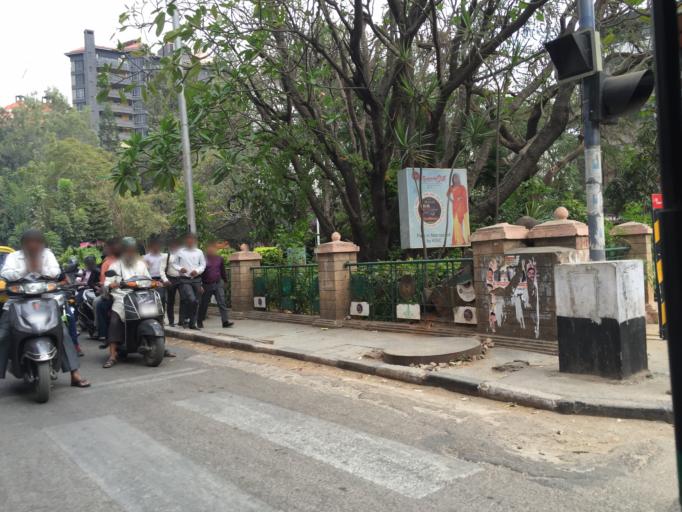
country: IN
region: Karnataka
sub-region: Bangalore Urban
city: Bangalore
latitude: 12.9744
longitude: 77.6111
